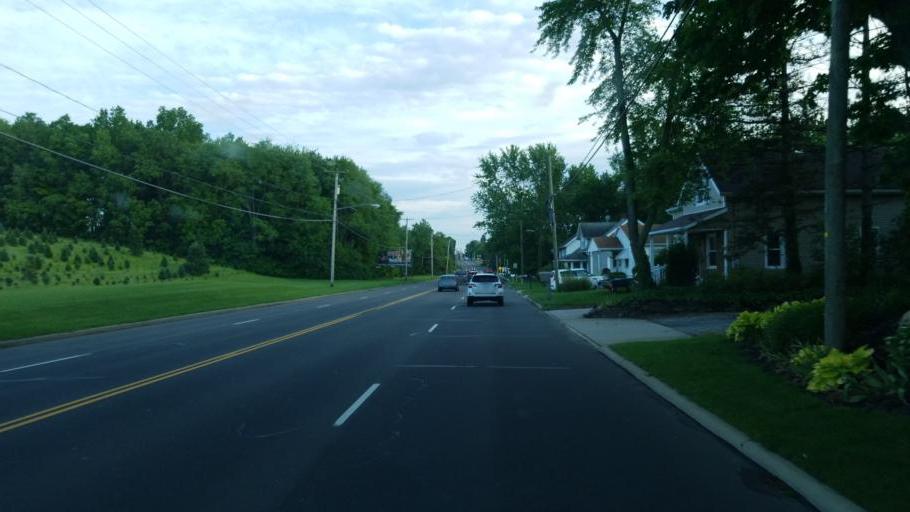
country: US
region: Ohio
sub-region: Stark County
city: Greentown
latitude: 40.9185
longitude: -81.4048
